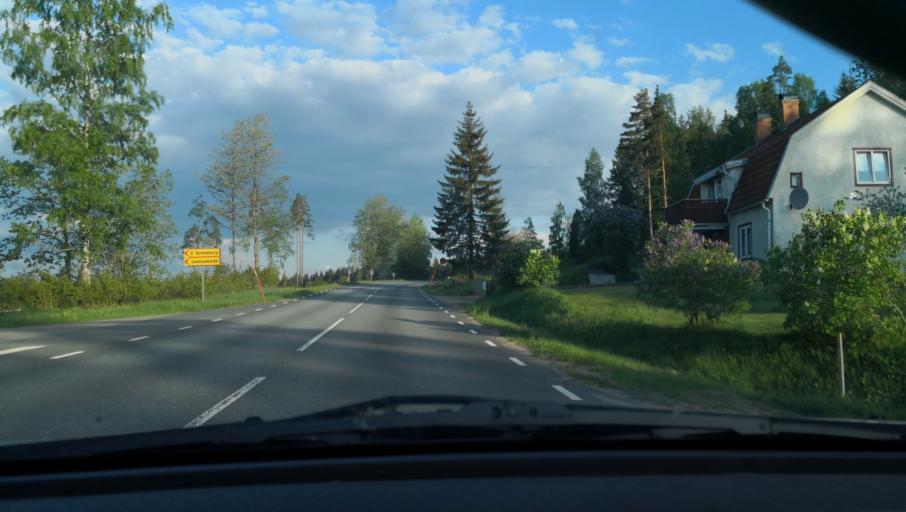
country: SE
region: Joenkoeping
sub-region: Vetlanda Kommun
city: Landsbro
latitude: 57.3783
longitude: 14.8613
